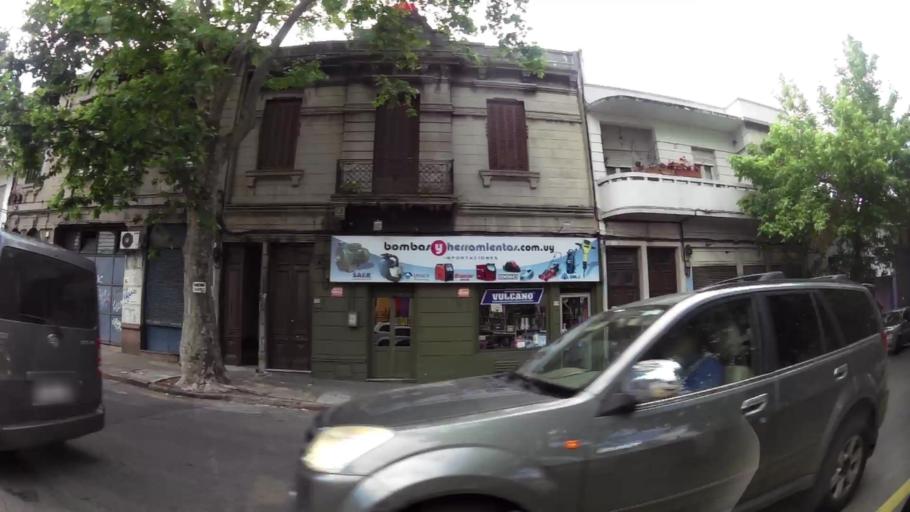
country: UY
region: Montevideo
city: Montevideo
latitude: -34.8758
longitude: -56.1854
